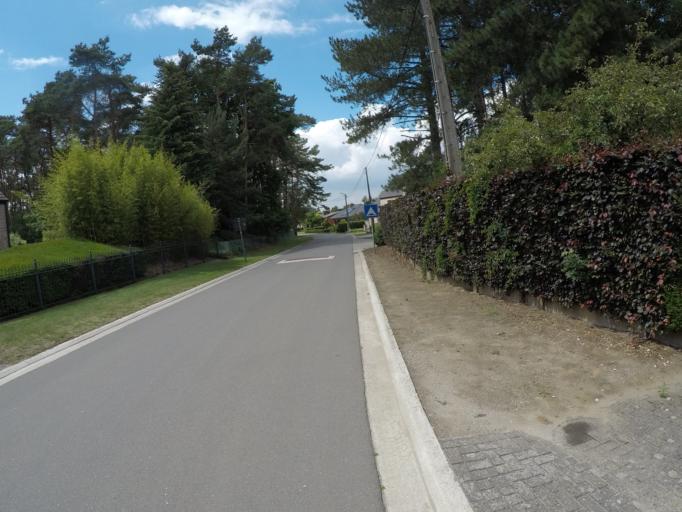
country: BE
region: Flanders
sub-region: Provincie Antwerpen
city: Lille
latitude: 51.2673
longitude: 4.7961
